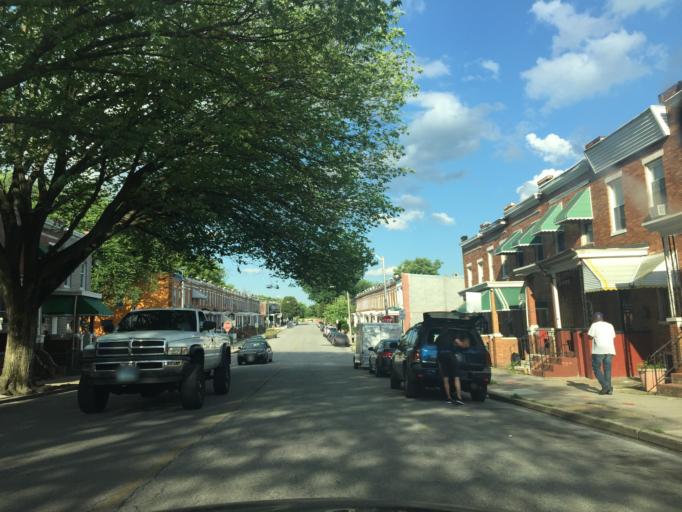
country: US
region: Maryland
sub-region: City of Baltimore
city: Baltimore
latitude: 39.3037
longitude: -76.5818
